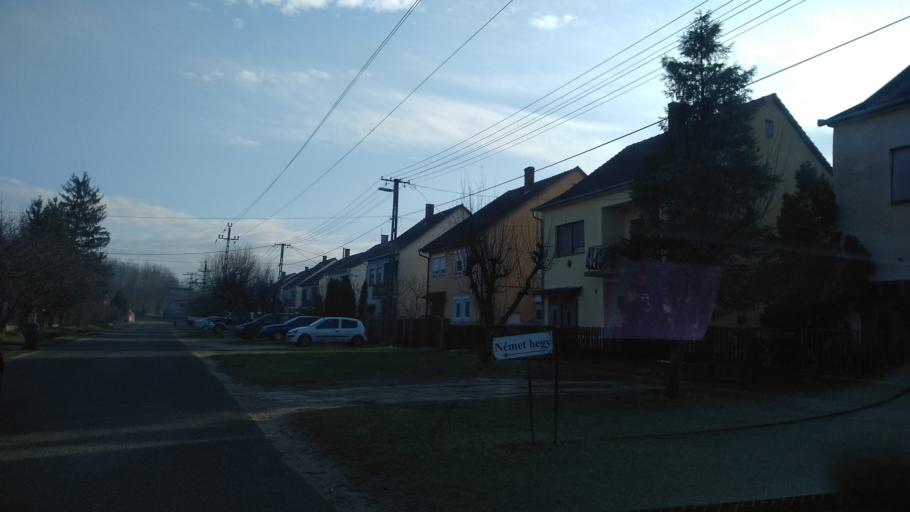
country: HU
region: Somogy
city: Barcs
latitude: 45.9663
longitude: 17.4720
